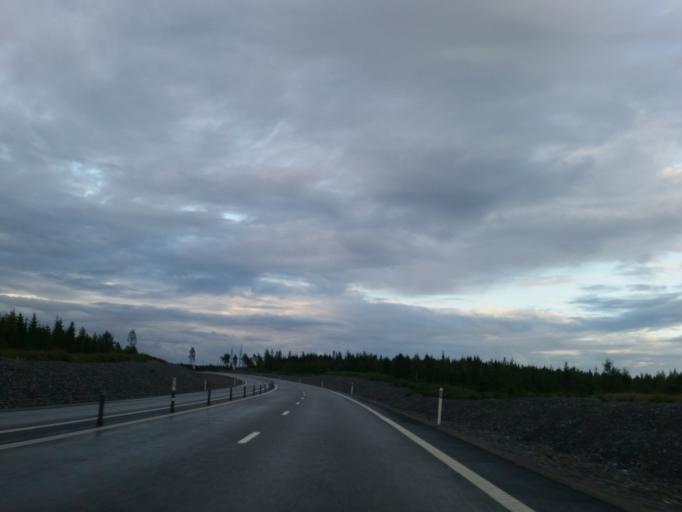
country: SE
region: Vaesterbotten
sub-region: Umea Kommun
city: Umea
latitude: 63.8553
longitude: 20.2619
